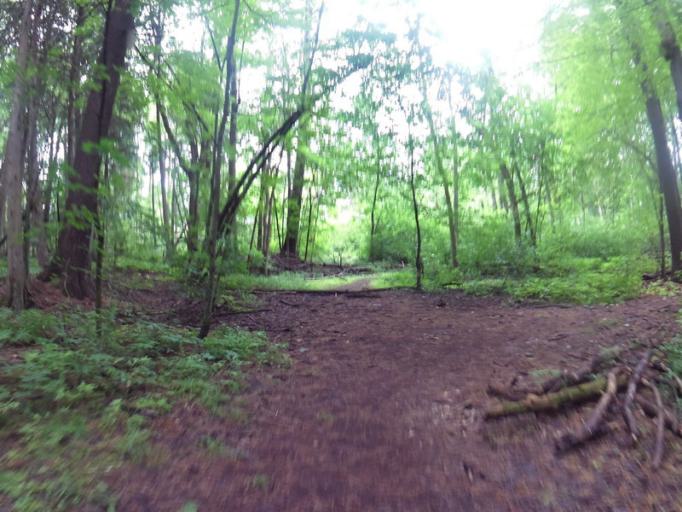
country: CA
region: Ontario
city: Ottawa
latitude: 45.3197
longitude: -75.7254
